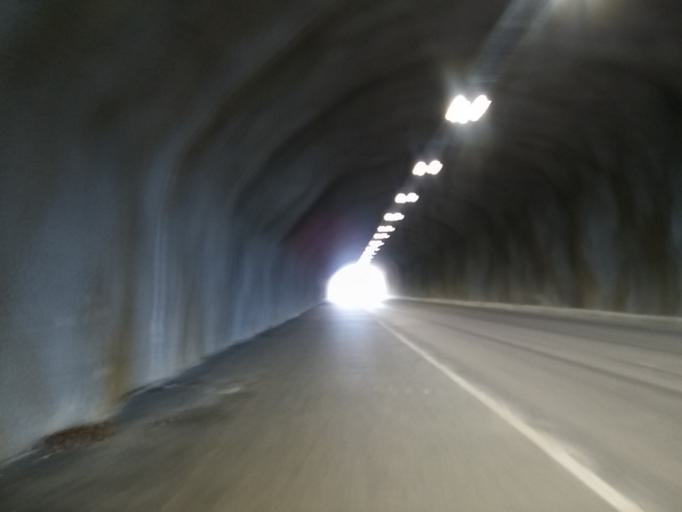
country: NO
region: Sor-Trondelag
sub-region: Malvik
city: Hommelvik
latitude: 63.4269
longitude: 10.7491
